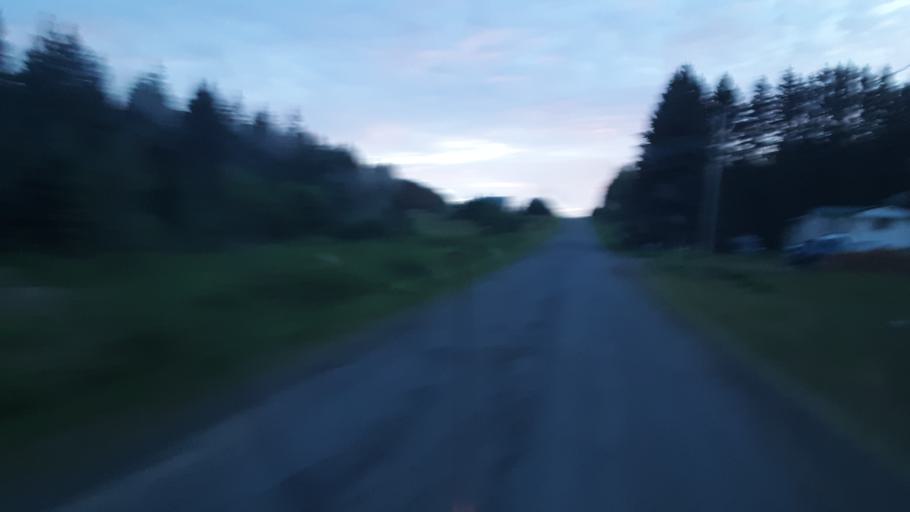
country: US
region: Maine
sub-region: Aroostook County
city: Caribou
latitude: 46.8580
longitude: -68.0921
